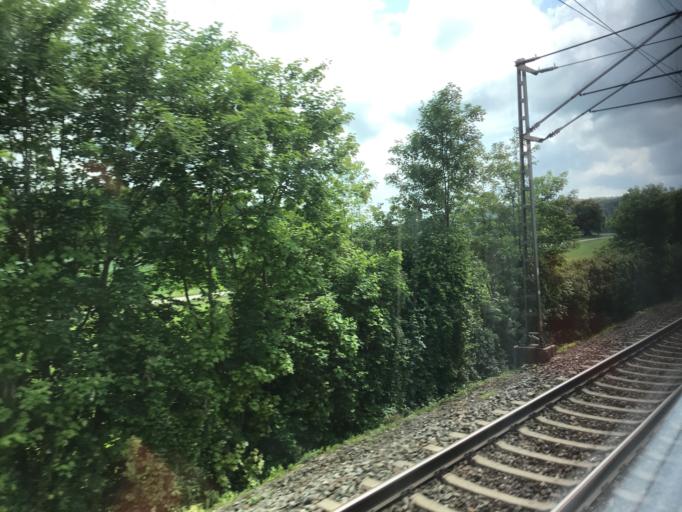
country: DE
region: Baden-Wuerttemberg
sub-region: Tuebingen Region
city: Lonsee
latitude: 48.5317
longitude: 9.9282
